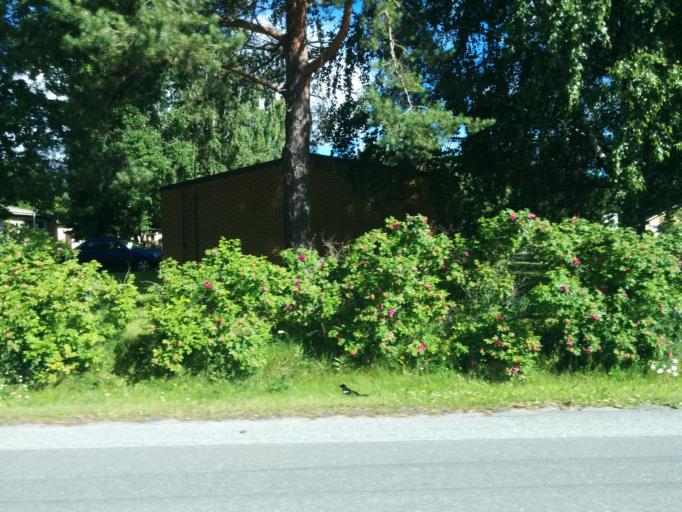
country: FI
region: Pirkanmaa
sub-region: Tampere
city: Orivesi
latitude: 61.6746
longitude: 24.3610
